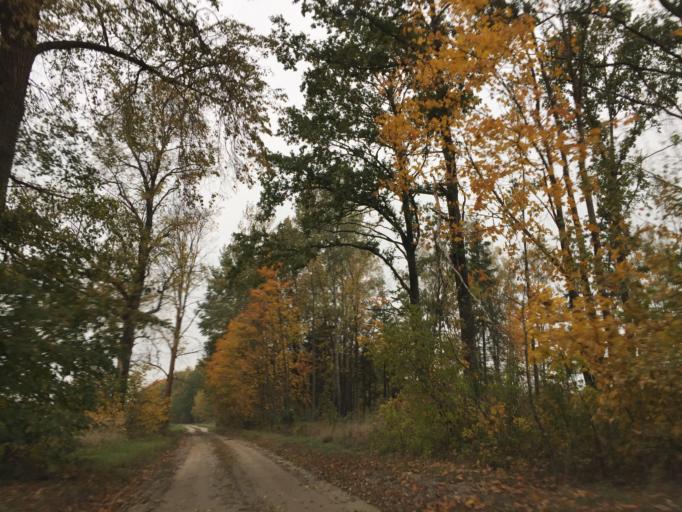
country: LV
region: Dobeles Rajons
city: Dobele
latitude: 56.6718
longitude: 23.4700
